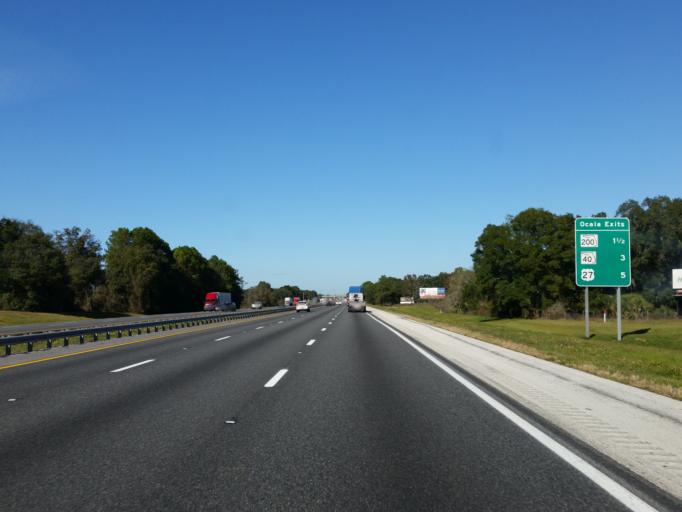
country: US
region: Florida
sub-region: Marion County
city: Ocala
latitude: 29.1233
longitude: -82.1847
